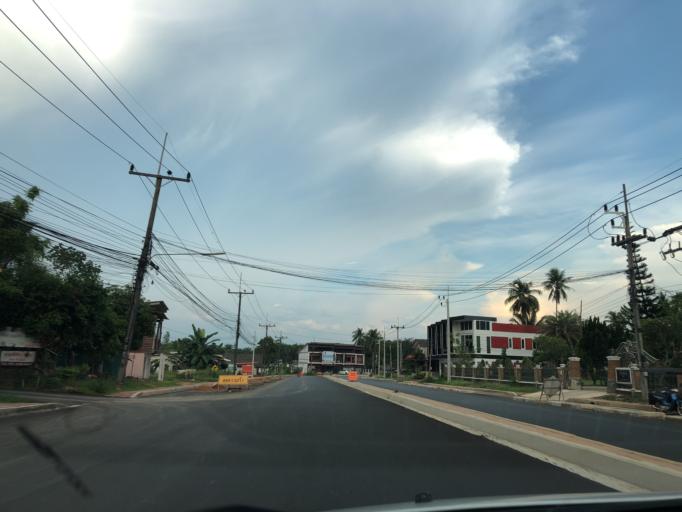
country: TH
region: Phangnga
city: Ban Ao Nang
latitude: 8.0703
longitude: 98.8395
